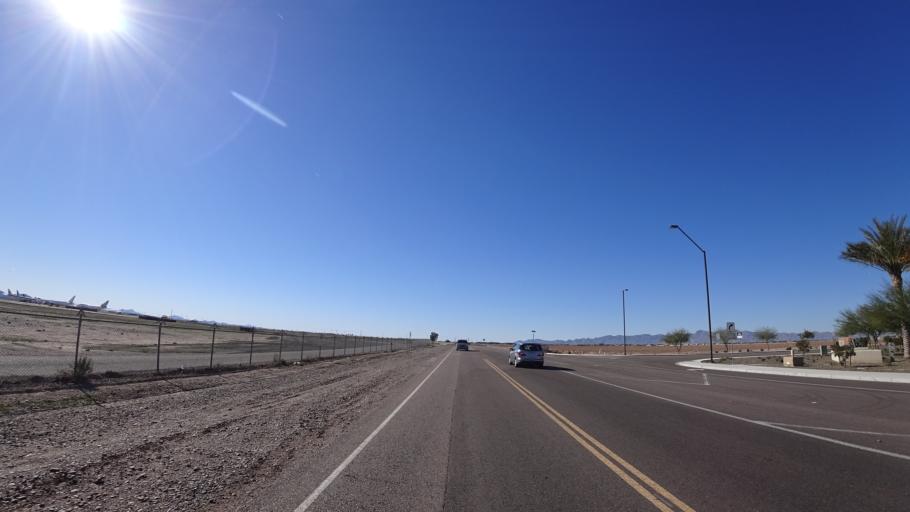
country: US
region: Arizona
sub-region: Maricopa County
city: Goodyear
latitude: 33.4354
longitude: -112.3686
